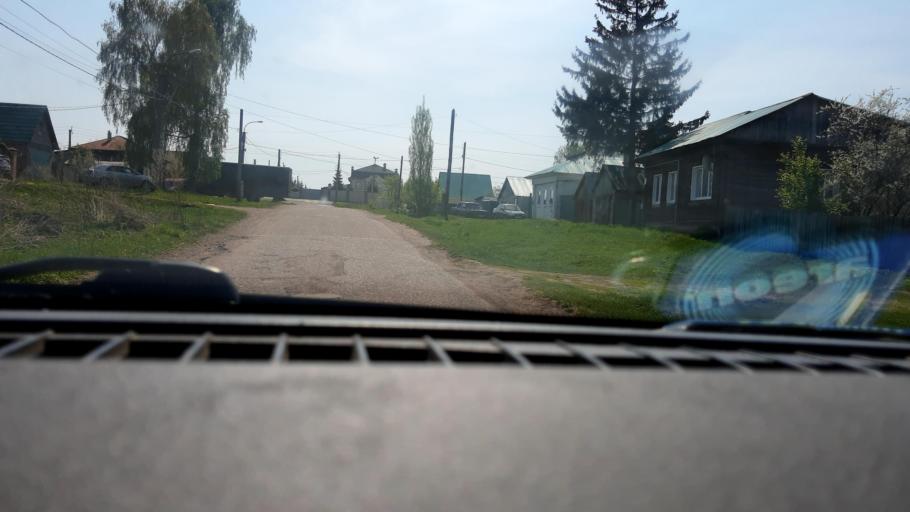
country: RU
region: Bashkortostan
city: Blagoveshchensk
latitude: 55.0236
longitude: 55.9808
